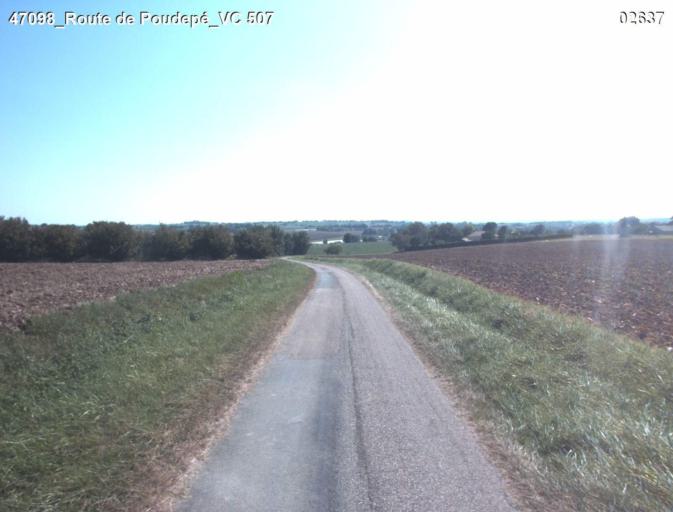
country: FR
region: Aquitaine
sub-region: Departement du Lot-et-Garonne
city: Nerac
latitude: 44.0973
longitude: 0.4002
